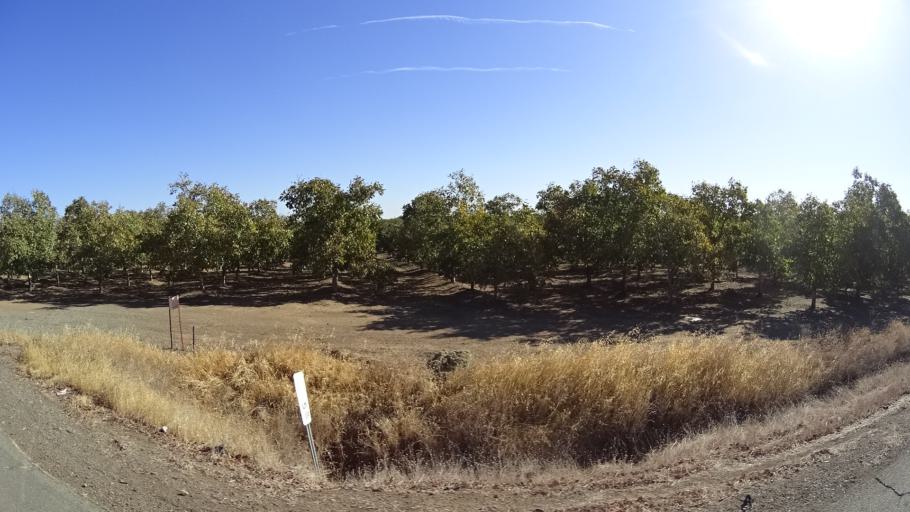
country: US
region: California
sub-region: Yolo County
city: Winters
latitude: 38.5049
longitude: -122.0187
